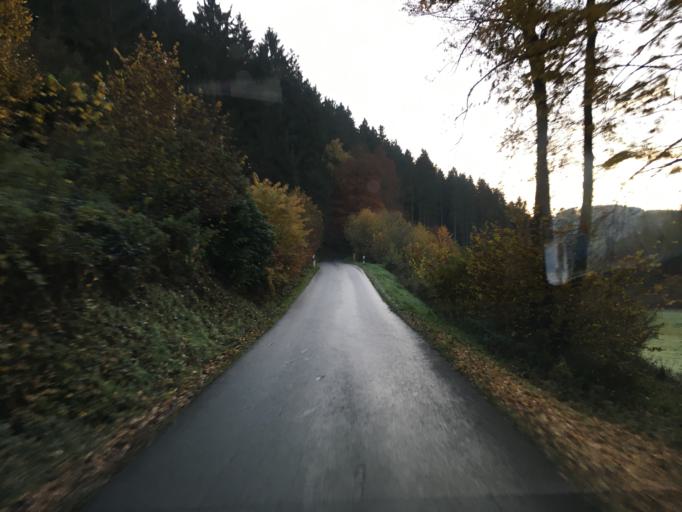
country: DE
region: North Rhine-Westphalia
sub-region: Regierungsbezirk Arnsberg
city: Nachrodt-Wiblingwerde
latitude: 51.2842
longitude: 7.6009
